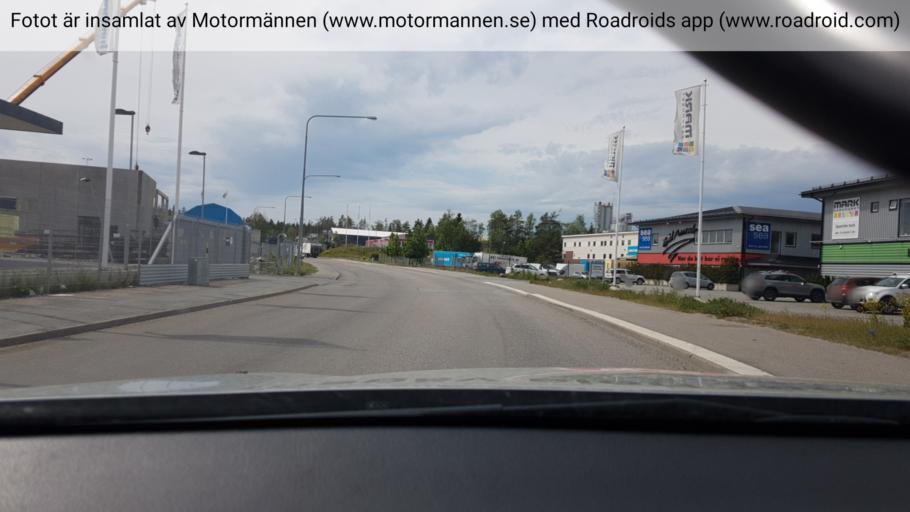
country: SE
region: Stockholm
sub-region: Haninge Kommun
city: Handen
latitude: 59.2030
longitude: 18.1235
